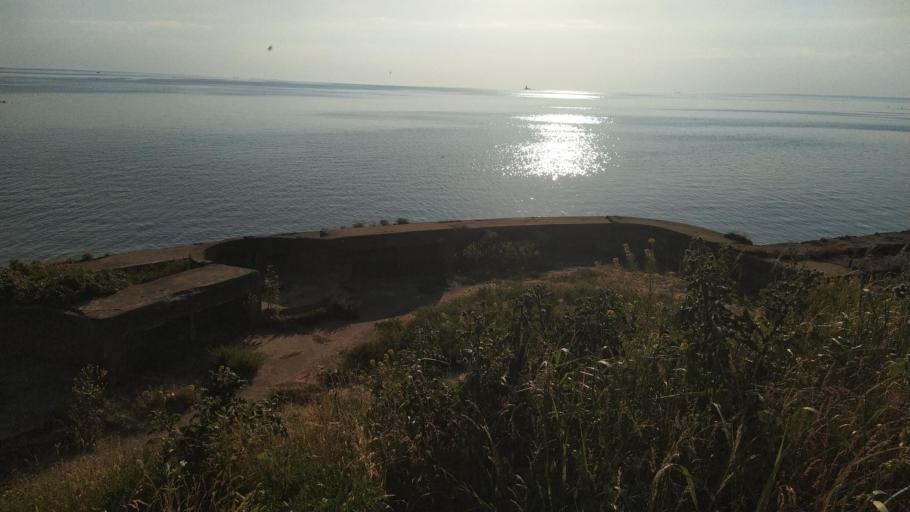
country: RU
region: St.-Petersburg
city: Bol'shaya Izhora
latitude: 60.0306
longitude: 29.6349
